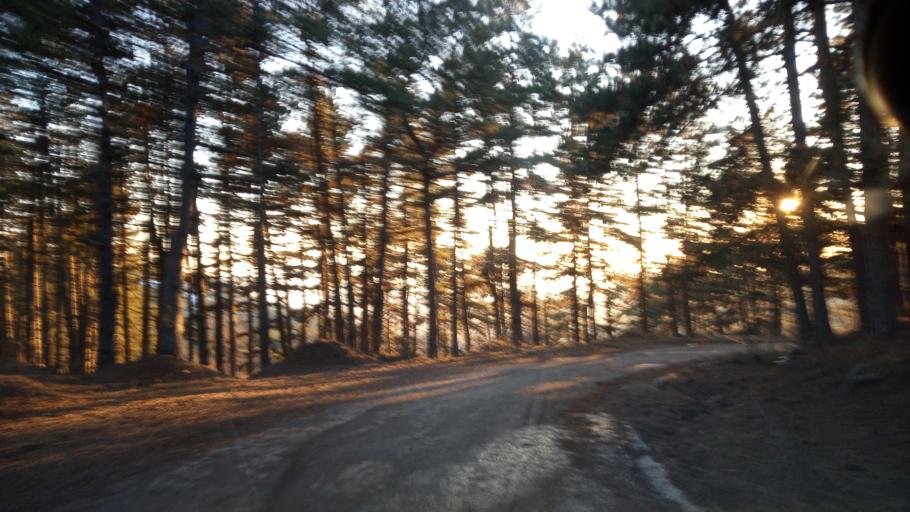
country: BG
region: Sofia-Capital
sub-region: Stolichna Obshtina
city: Bukhovo
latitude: 42.7917
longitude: 23.5274
